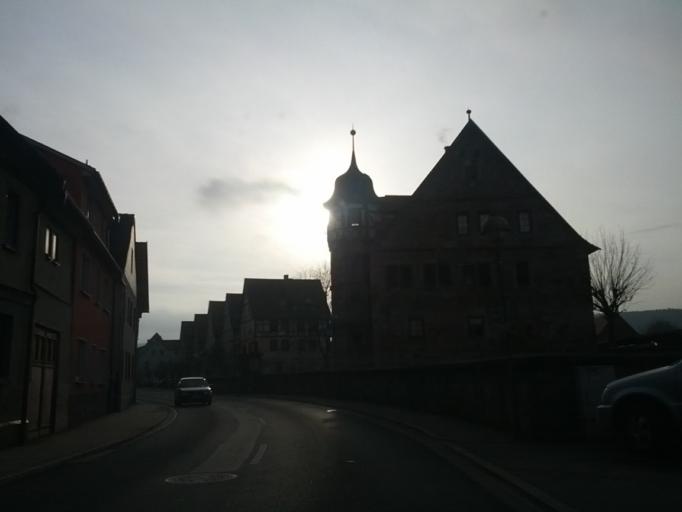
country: DE
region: Thuringia
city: Wasungen
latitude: 50.6656
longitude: 10.3664
